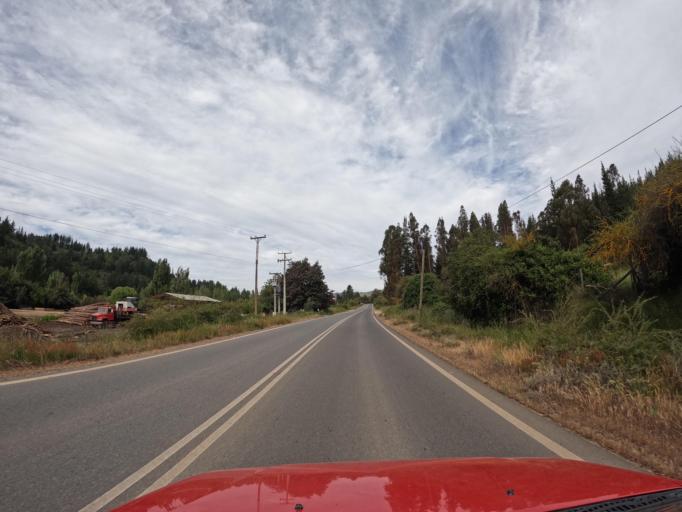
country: CL
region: Maule
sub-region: Provincia de Talca
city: Talca
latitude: -35.3226
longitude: -71.9436
